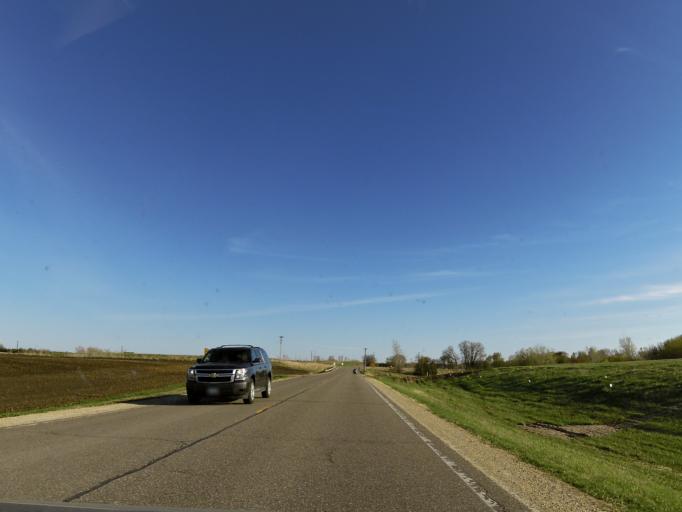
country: US
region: Minnesota
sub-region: Dakota County
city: Lakeville
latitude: 44.6142
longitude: -93.2632
